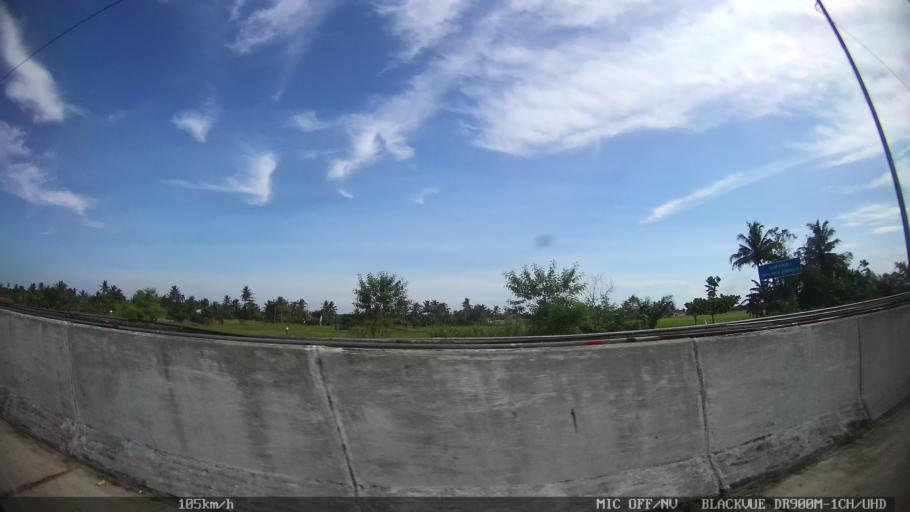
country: ID
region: North Sumatra
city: Sunggal
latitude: 3.6439
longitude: 98.5611
